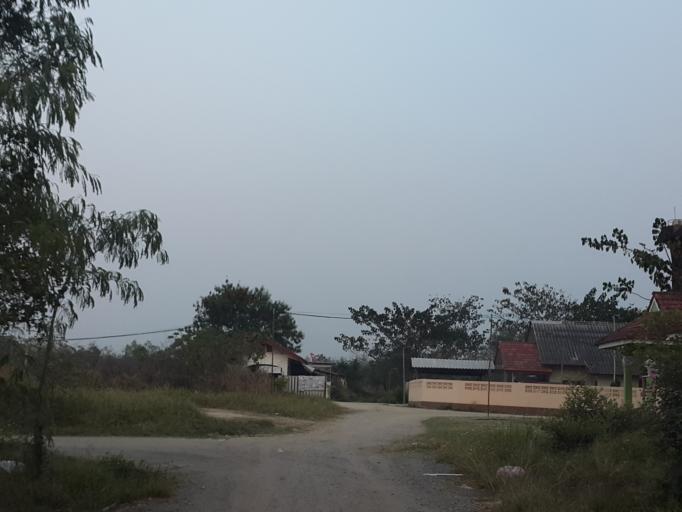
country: TH
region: Chiang Mai
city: San Kamphaeng
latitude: 18.7758
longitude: 99.0762
